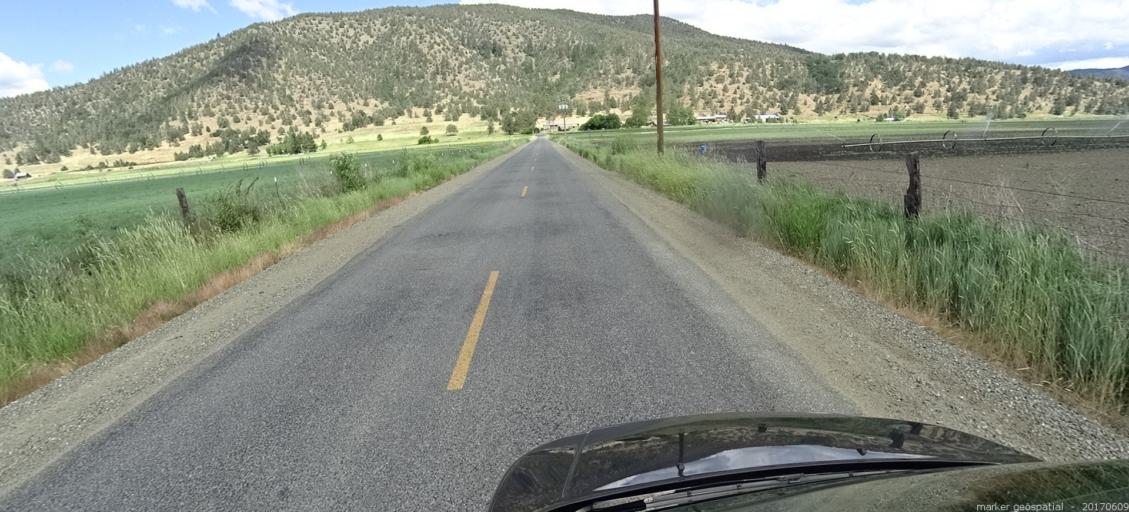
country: US
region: California
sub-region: Siskiyou County
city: Yreka
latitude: 41.5195
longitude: -122.8475
